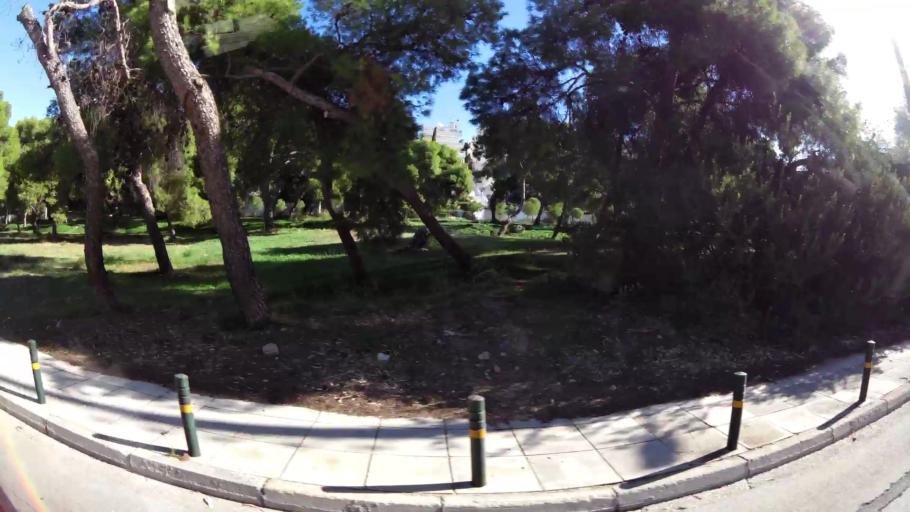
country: GR
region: Attica
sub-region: Nomarchia Anatolikis Attikis
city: Vouliagmeni
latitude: 37.8169
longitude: 23.7720
